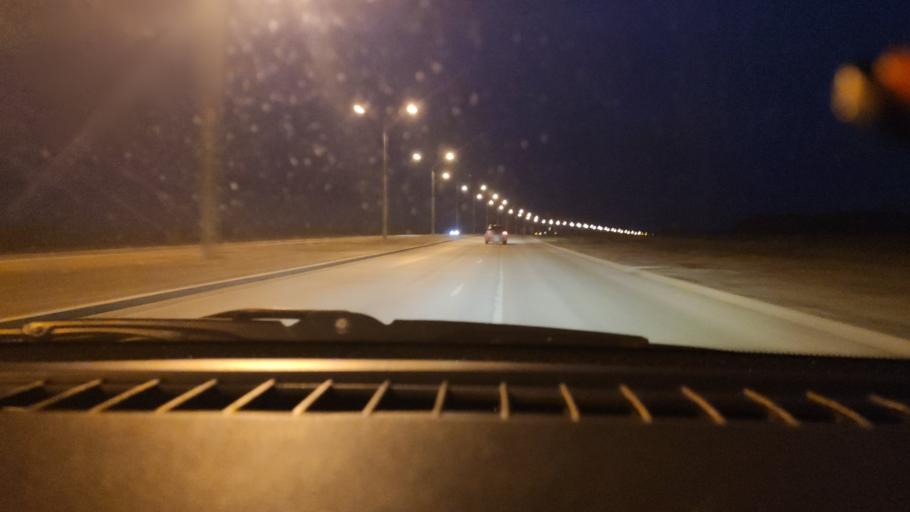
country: RU
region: Perm
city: Perm
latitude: 58.0070
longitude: 56.3474
